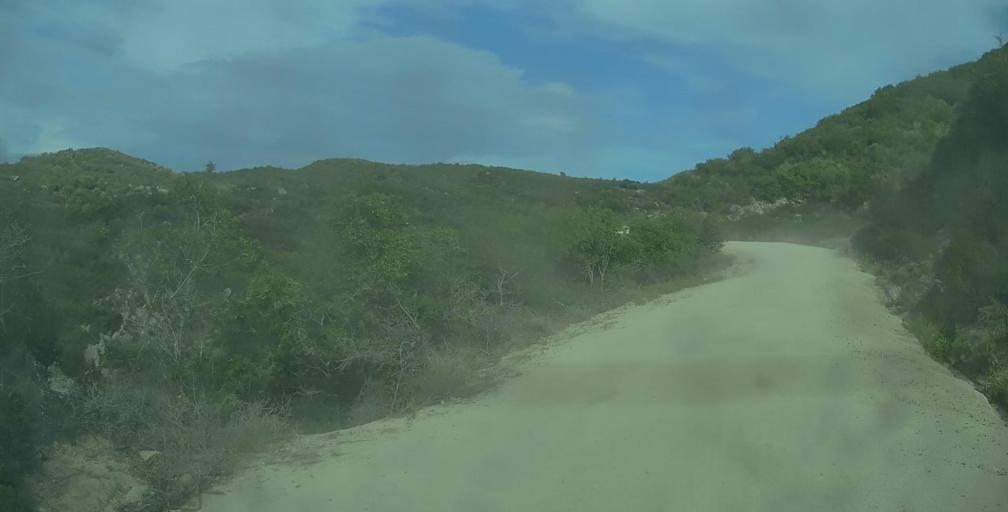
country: GR
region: Central Macedonia
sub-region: Nomos Chalkidikis
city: Sykia
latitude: 39.9897
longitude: 23.9142
